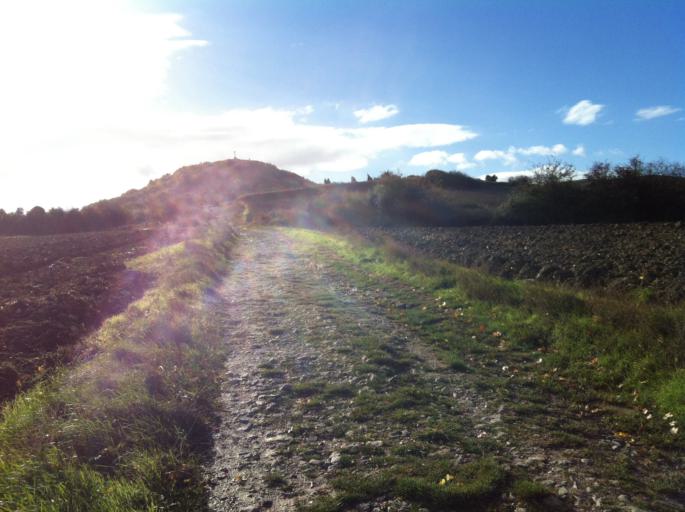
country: ES
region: Basque Country
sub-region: Provincia de Alava
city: Gasteiz / Vitoria
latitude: 42.8243
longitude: -2.6651
